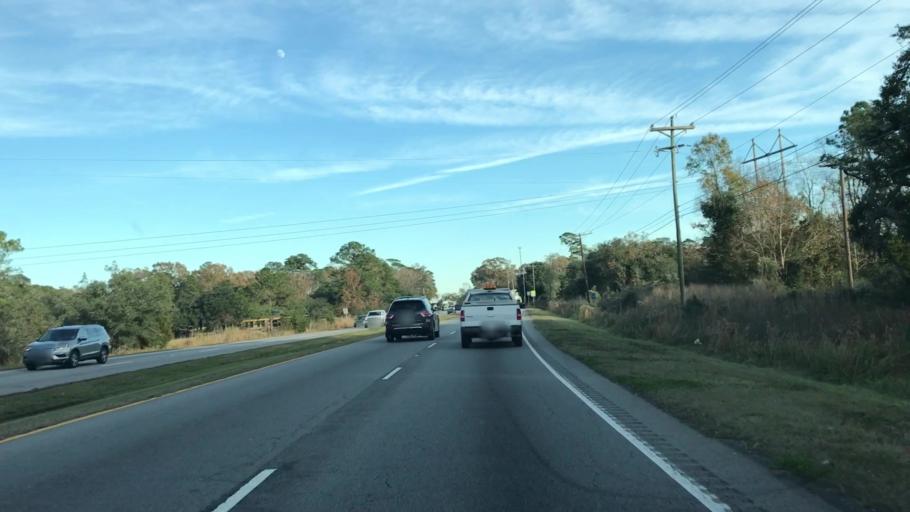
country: US
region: South Carolina
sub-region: Charleston County
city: Shell Point
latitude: 32.7942
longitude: -80.0594
